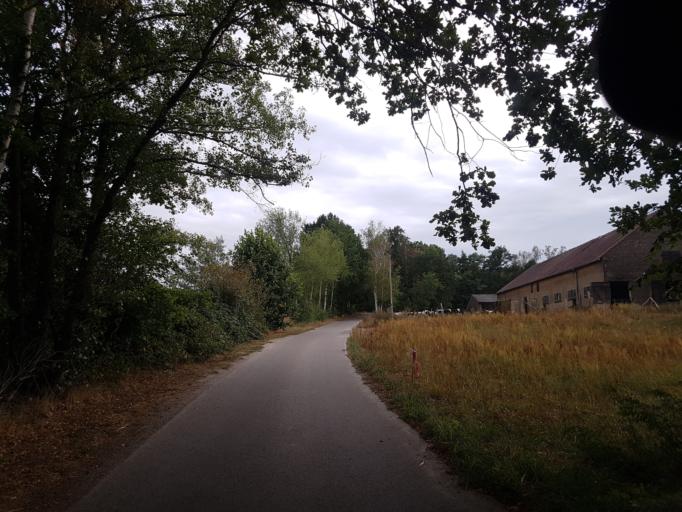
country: DE
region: Brandenburg
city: Calau
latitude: 51.7176
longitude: 13.9472
